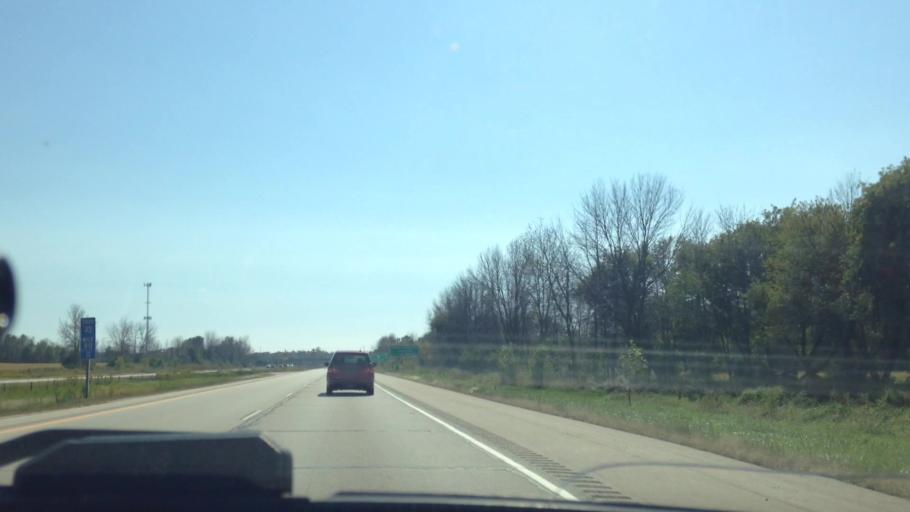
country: US
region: Wisconsin
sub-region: Ozaukee County
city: Grafton
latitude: 43.2878
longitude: -87.9212
